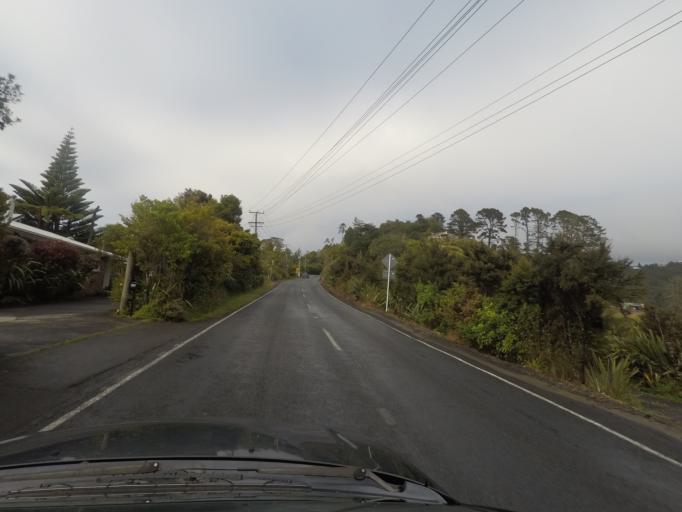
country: NZ
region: Auckland
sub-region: Auckland
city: Titirangi
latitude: -36.9248
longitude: 174.5828
